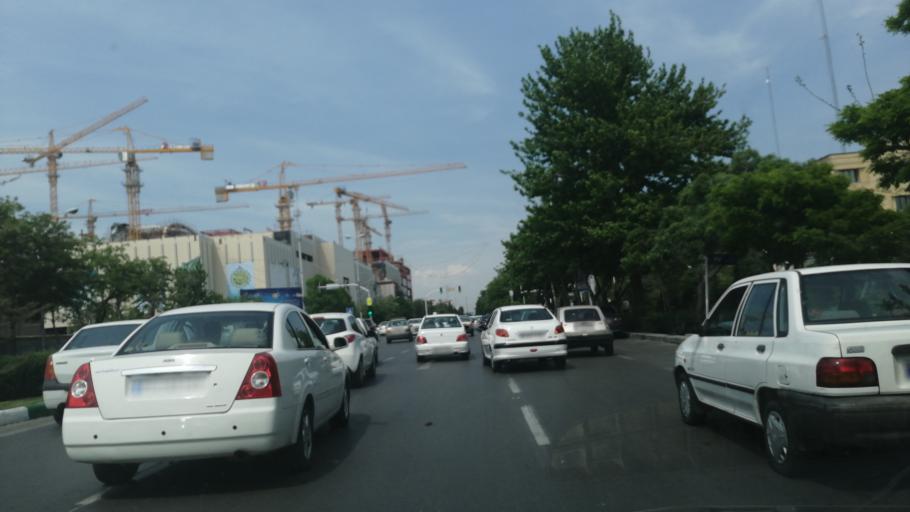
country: IR
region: Razavi Khorasan
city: Mashhad
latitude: 36.3141
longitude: 59.5596
